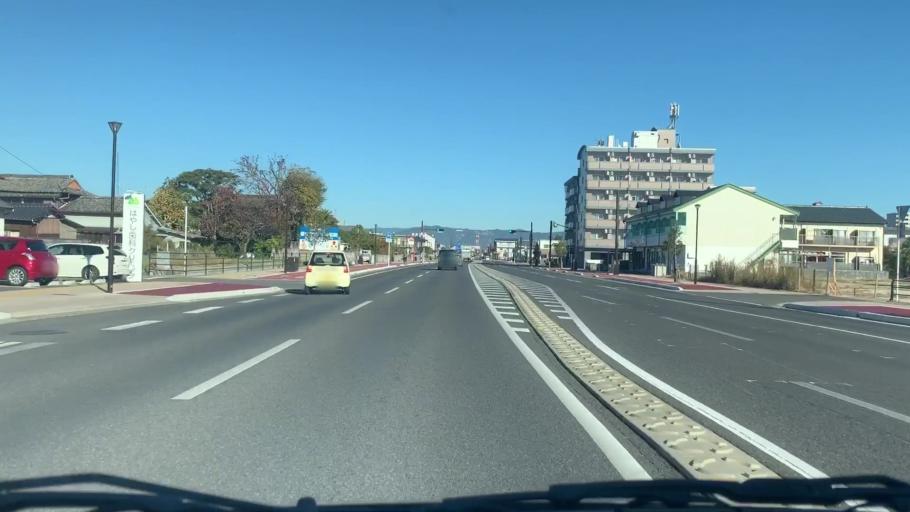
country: JP
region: Saga Prefecture
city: Saga-shi
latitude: 33.2456
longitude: 130.2932
